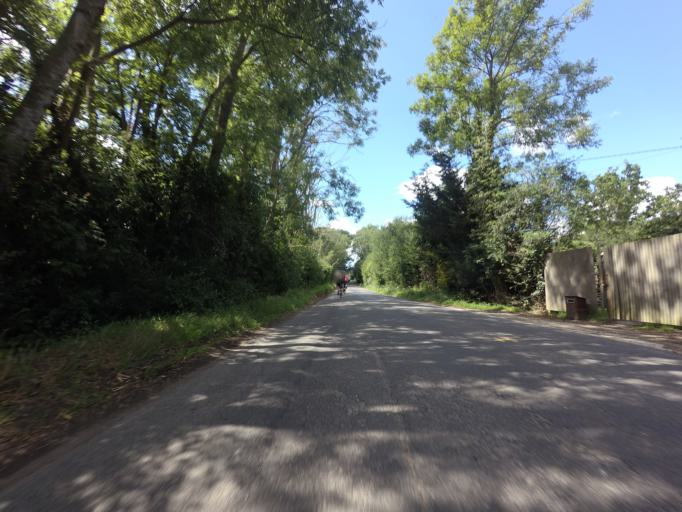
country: GB
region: England
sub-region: East Sussex
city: Horam
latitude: 50.8929
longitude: 0.1859
